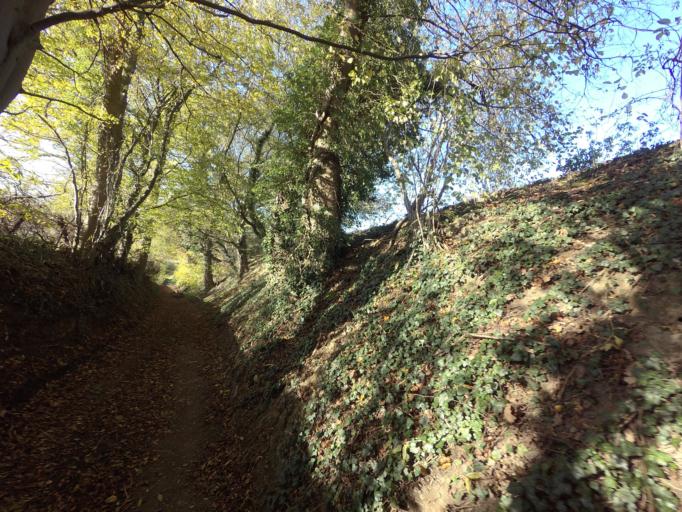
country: NL
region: Limburg
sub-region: Gemeente Simpelveld
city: Simpelveld
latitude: 50.8056
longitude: 5.9663
